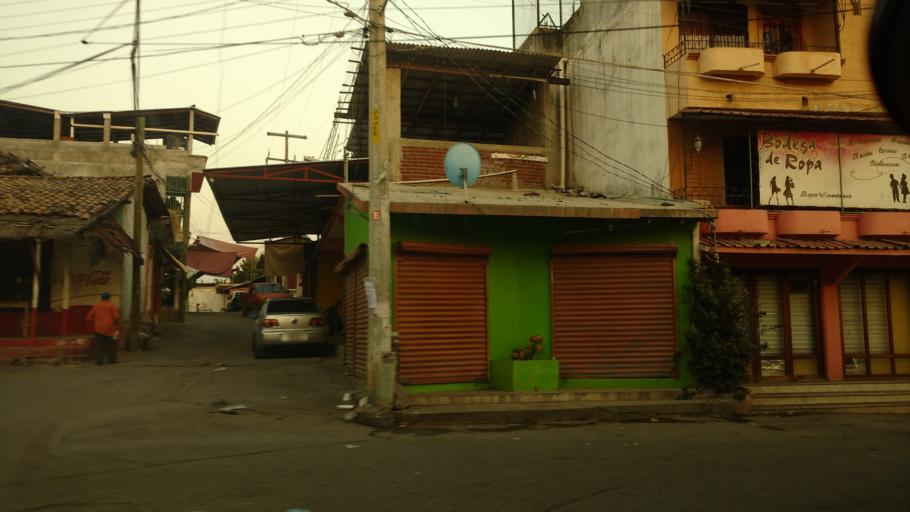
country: MX
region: Guerrero
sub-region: Tecpan de Galeana
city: Villa Rotaria
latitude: 17.2694
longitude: -100.8915
